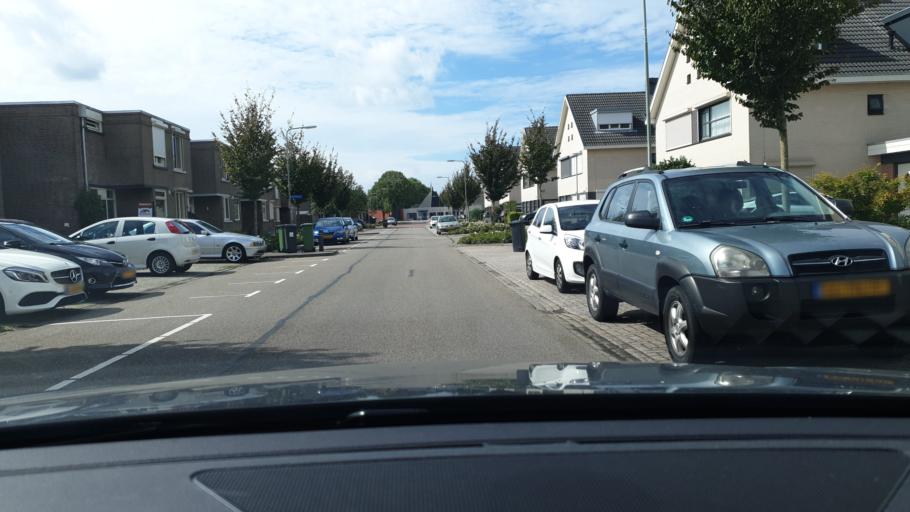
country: NL
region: Limburg
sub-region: Gemeente Venray
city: Venray
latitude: 51.5341
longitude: 5.9948
